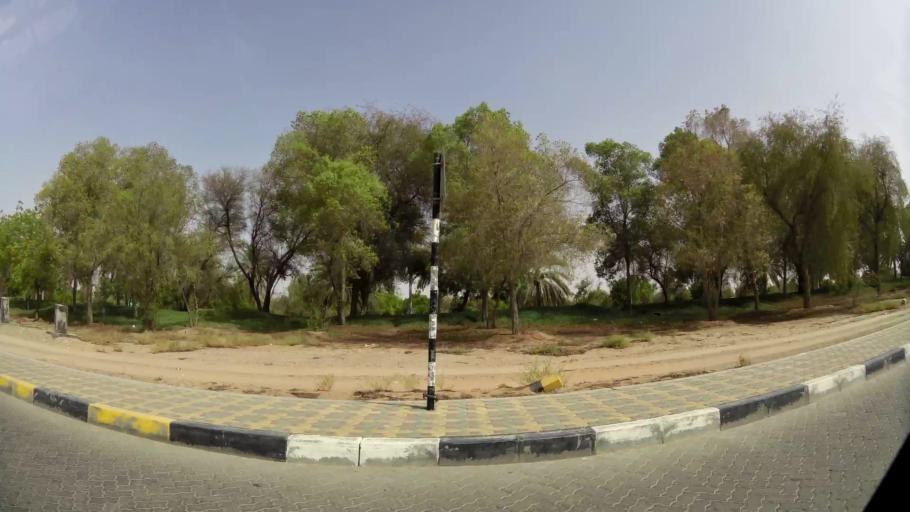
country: AE
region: Abu Dhabi
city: Al Ain
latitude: 24.1861
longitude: 55.6344
